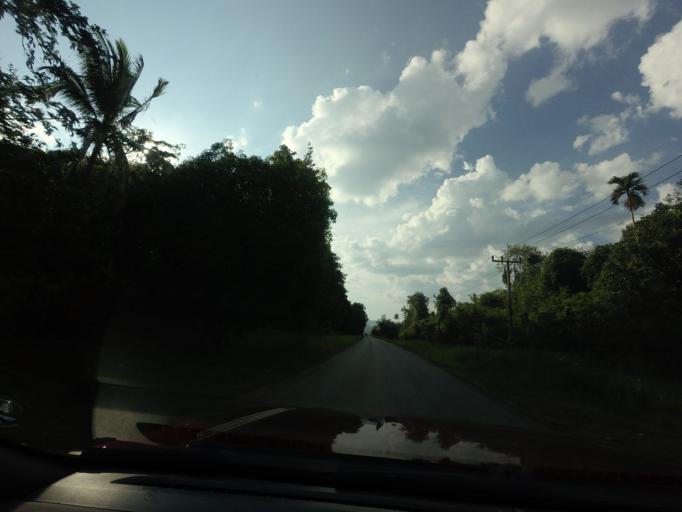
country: TH
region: Yala
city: Ban Nang Sata
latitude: 6.2150
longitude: 101.2323
